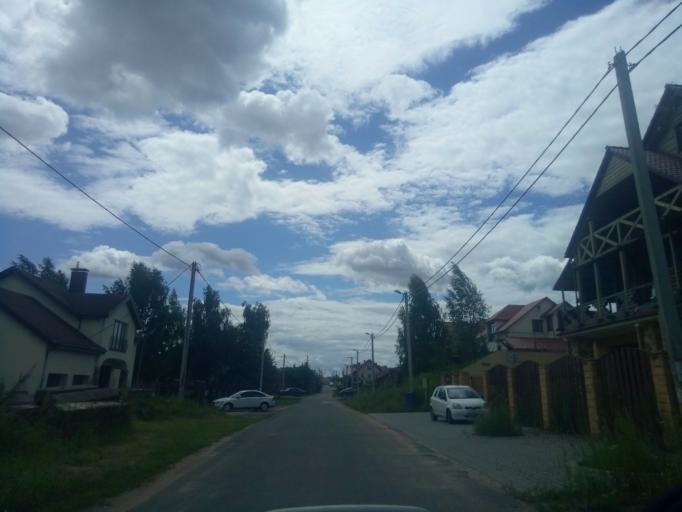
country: BY
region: Minsk
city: Zhdanovichy
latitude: 53.9393
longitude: 27.4023
